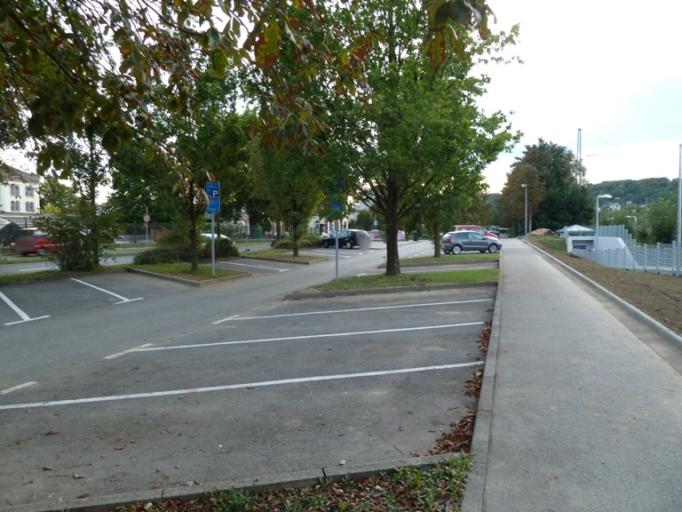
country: DE
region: Baden-Wuerttemberg
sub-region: Tuebingen Region
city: Tuebingen
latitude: 48.5152
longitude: 9.0558
